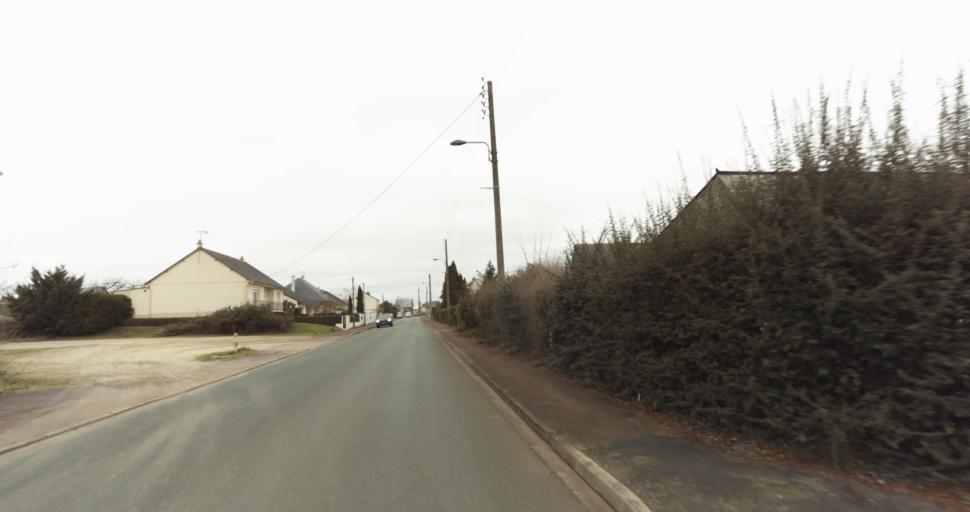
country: FR
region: Pays de la Loire
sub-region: Departement de Maine-et-Loire
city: Montreuil-Bellay
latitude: 47.1258
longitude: -0.1468
